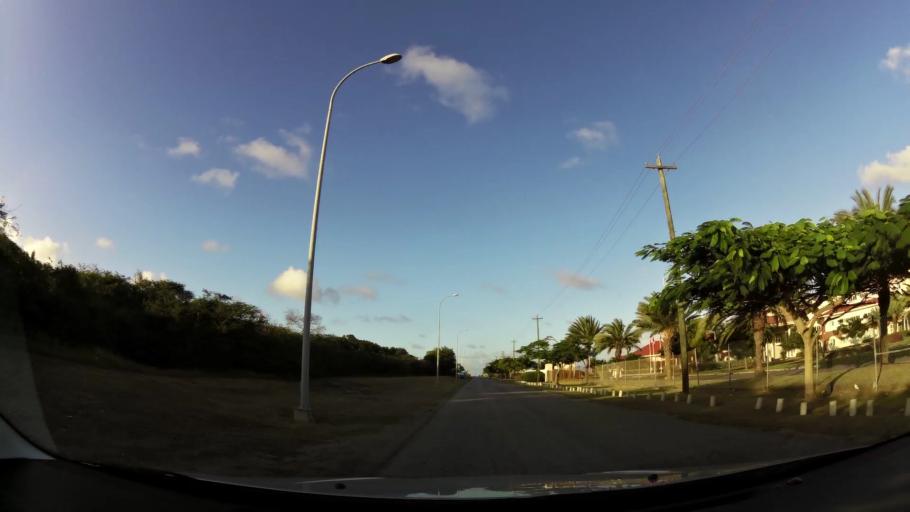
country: AG
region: Saint George
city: Piggotts
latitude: 17.1557
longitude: -61.7984
